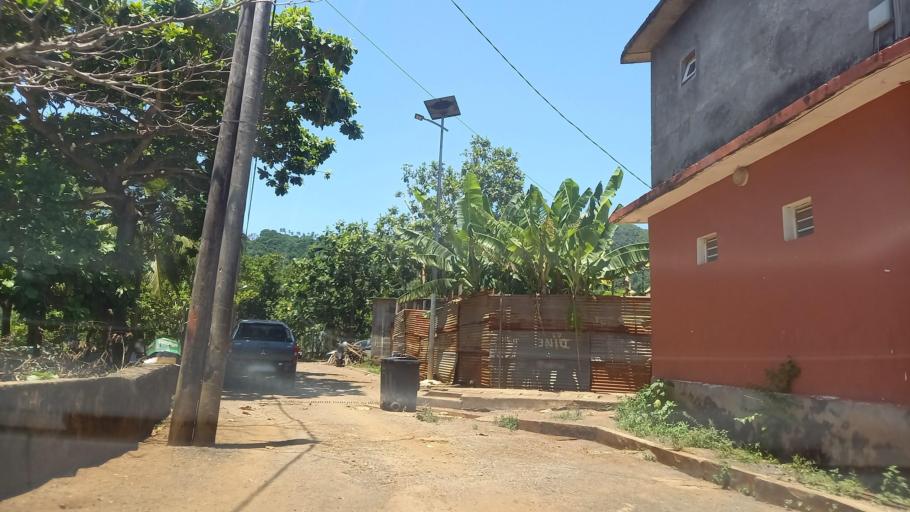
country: YT
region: Acoua
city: Acoua
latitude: -12.7269
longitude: 45.0579
